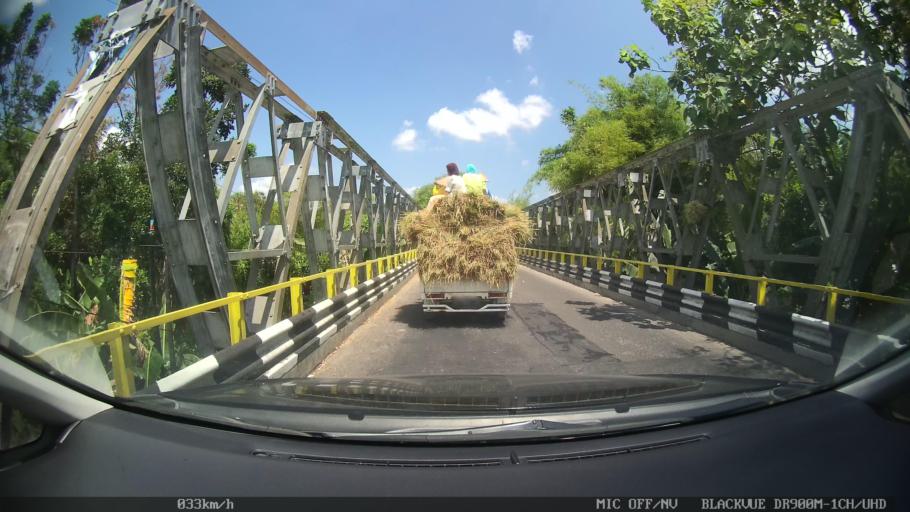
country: ID
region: Daerah Istimewa Yogyakarta
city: Sewon
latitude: -7.9030
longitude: 110.3838
